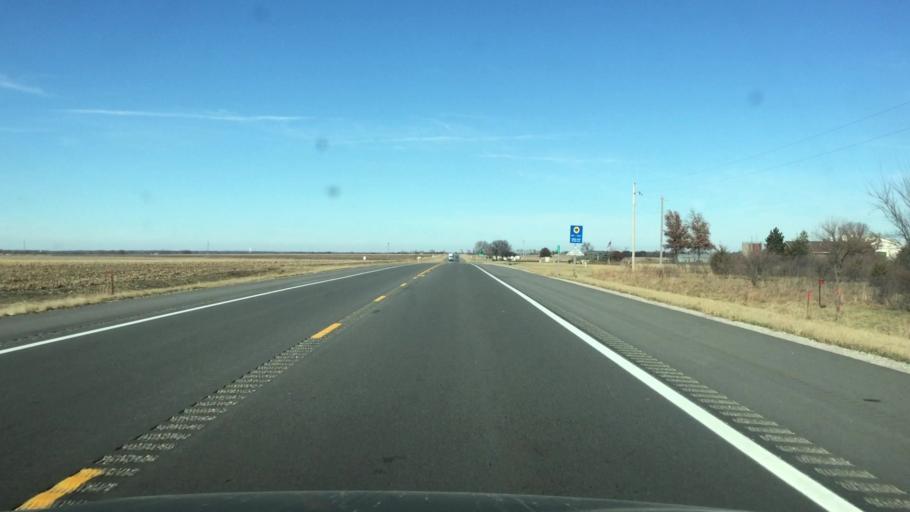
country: US
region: Kansas
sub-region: Anderson County
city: Garnett
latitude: 38.4294
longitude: -95.2486
